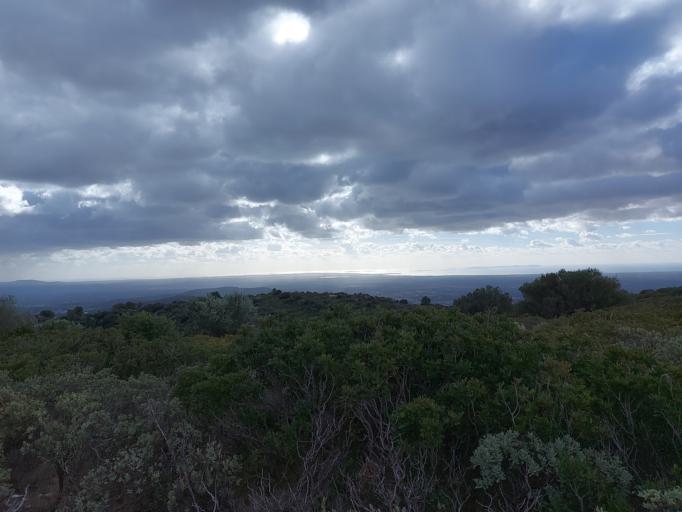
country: ES
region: Balearic Islands
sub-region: Illes Balears
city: Llucmajor
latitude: 39.5205
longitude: 2.9170
